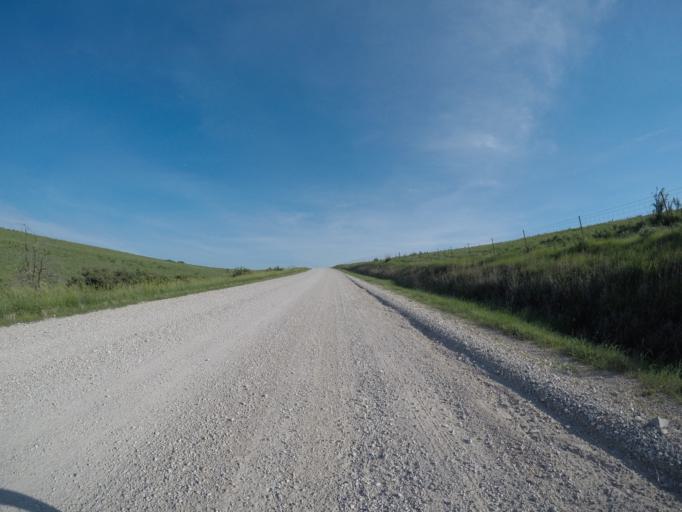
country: US
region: Kansas
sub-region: Riley County
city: Manhattan
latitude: 39.0524
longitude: -96.4960
